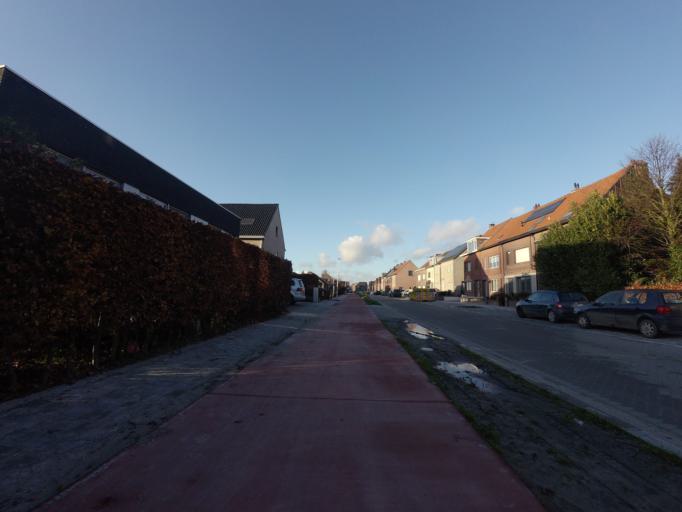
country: BE
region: Flanders
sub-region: Provincie Antwerpen
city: Schelle
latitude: 51.1223
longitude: 4.3450
